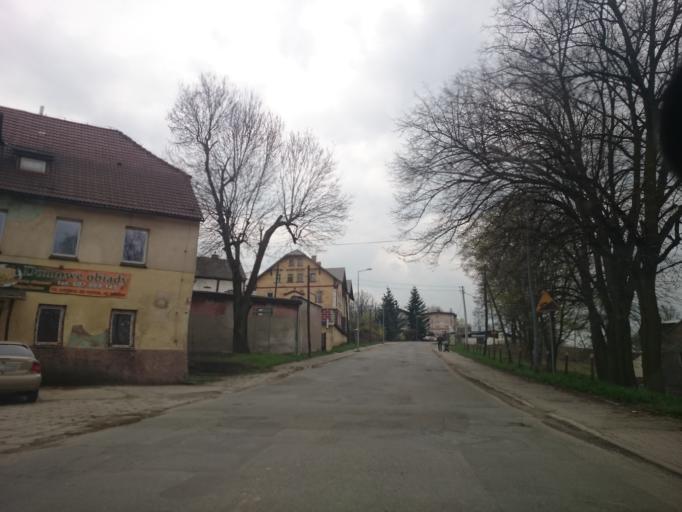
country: PL
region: Lower Silesian Voivodeship
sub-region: Powiat klodzki
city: Bystrzyca Klodzka
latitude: 50.2947
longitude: 16.6511
